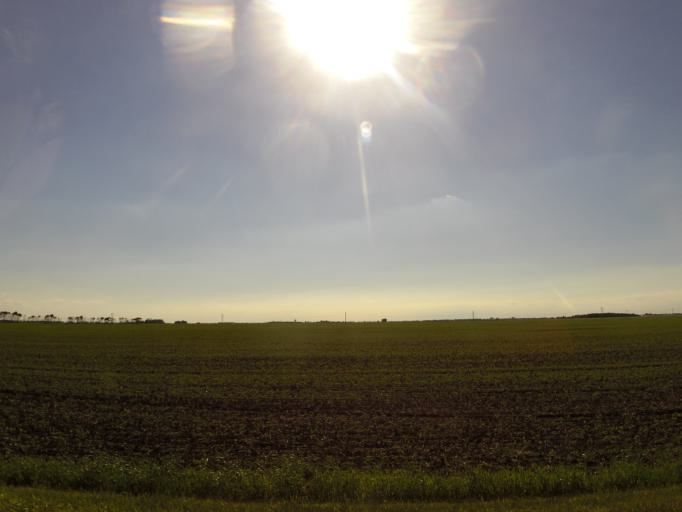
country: US
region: North Dakota
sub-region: Walsh County
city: Grafton
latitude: 48.4083
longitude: -97.2556
